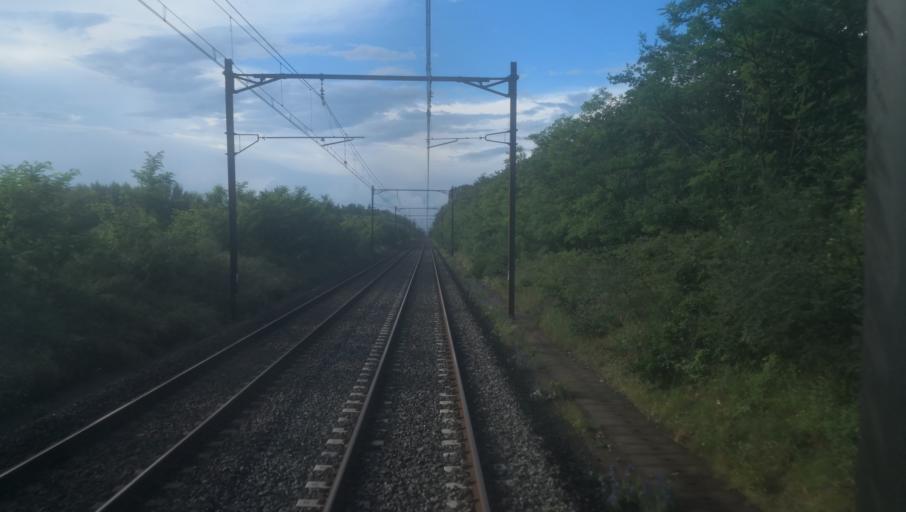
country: FR
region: Centre
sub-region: Departement du Loir-et-Cher
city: Nouan-le-Fuzelier
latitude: 47.4921
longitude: 2.0379
